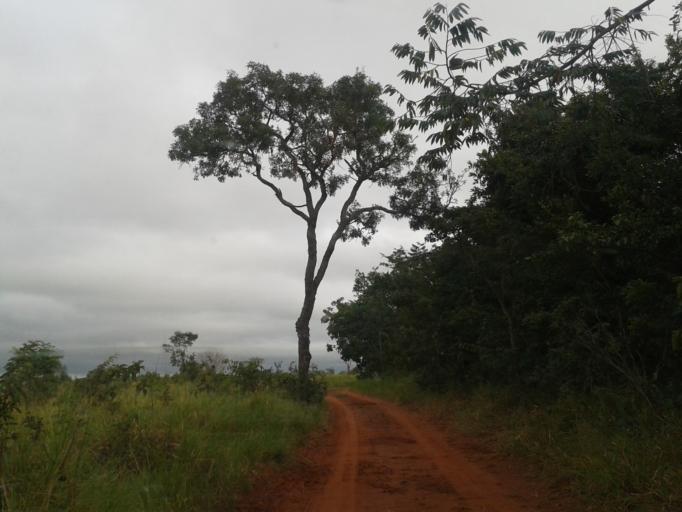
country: BR
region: Minas Gerais
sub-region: Campina Verde
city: Campina Verde
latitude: -19.4098
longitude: -49.6321
